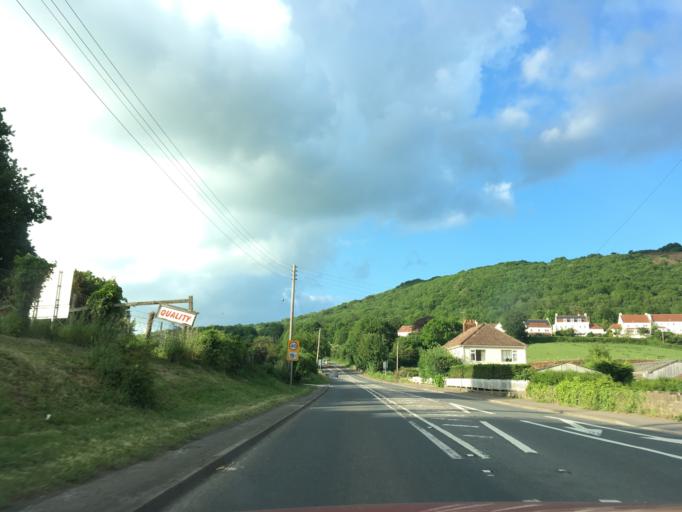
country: GB
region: England
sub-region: Somerset
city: Axbridge
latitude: 51.2898
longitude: -2.8341
